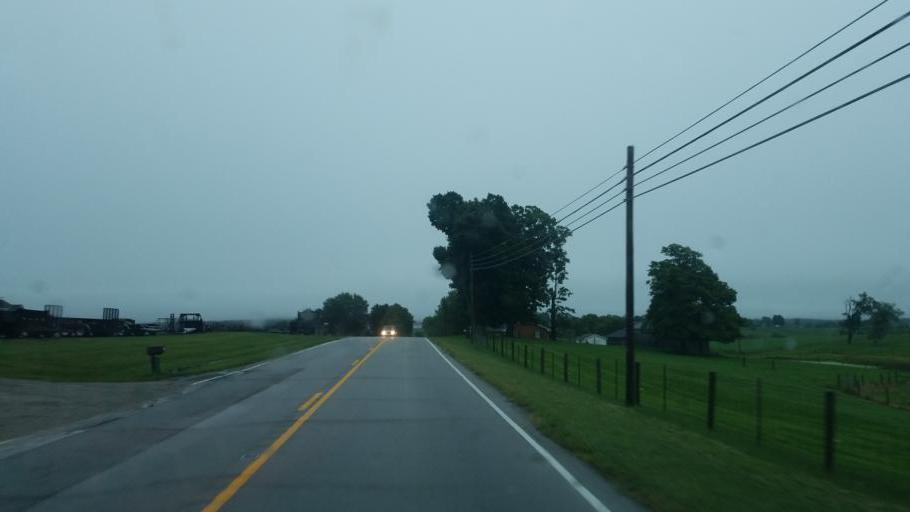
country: US
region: Kentucky
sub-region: Fleming County
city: Flemingsburg
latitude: 38.3903
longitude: -83.6780
